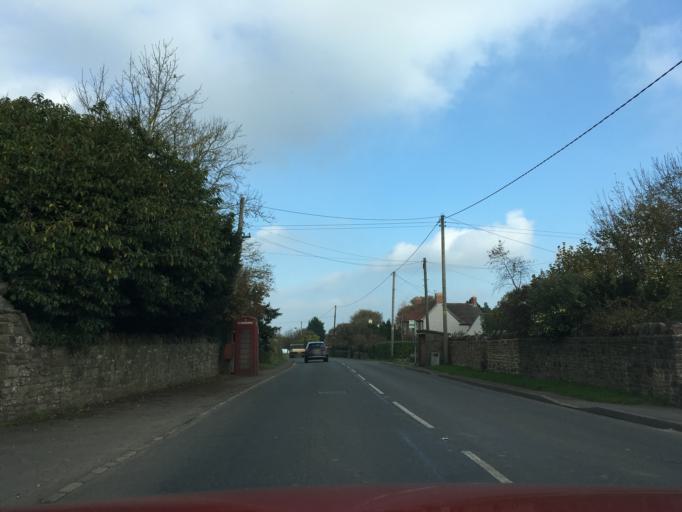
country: GB
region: England
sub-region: South Gloucestershire
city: Tytherington
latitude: 51.6002
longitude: -2.4404
